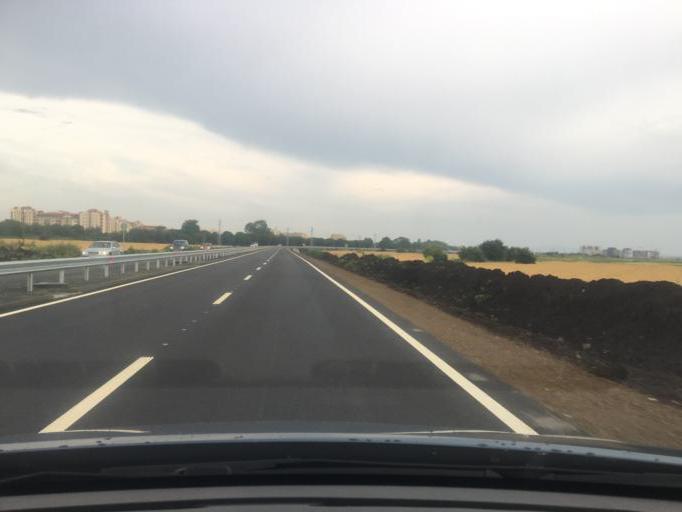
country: BG
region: Burgas
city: Aheloy
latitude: 42.6437
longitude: 27.6372
